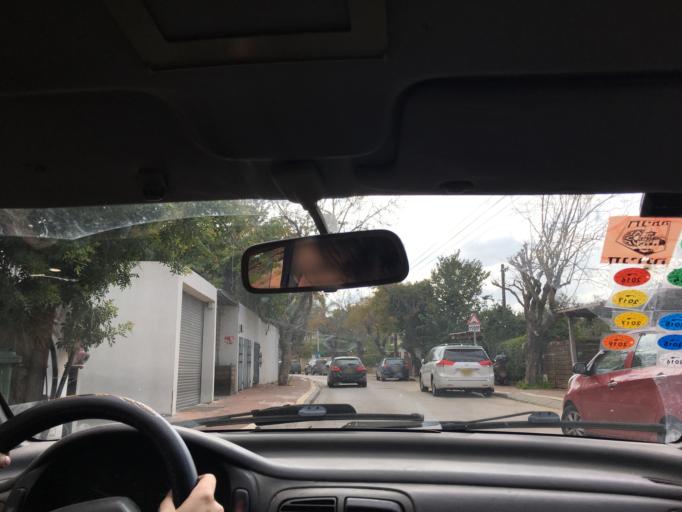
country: IL
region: Tel Aviv
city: Ramat HaSharon
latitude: 32.1429
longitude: 34.8306
